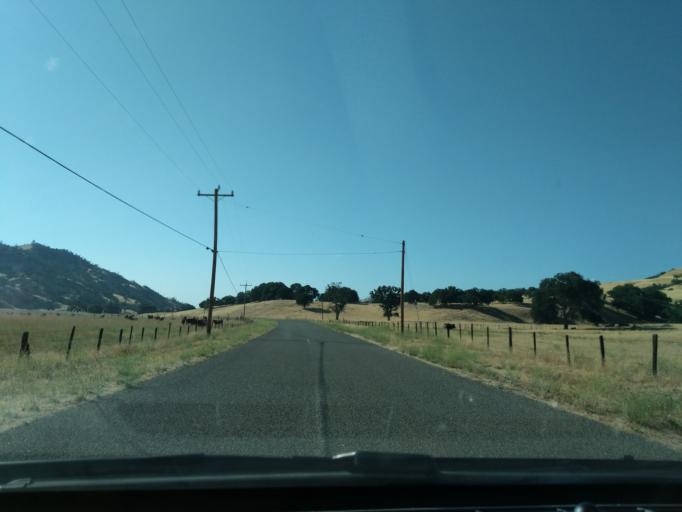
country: US
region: California
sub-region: San Luis Obispo County
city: San Miguel
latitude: 36.1264
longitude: -120.7382
